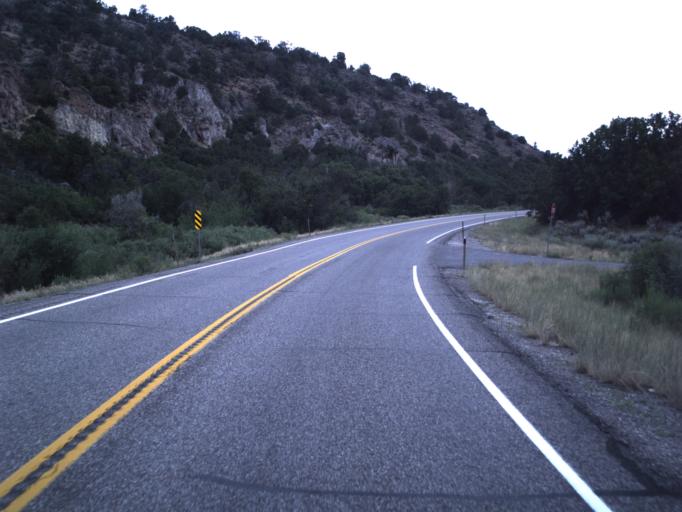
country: US
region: Utah
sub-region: Sevier County
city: Richfield
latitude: 38.7360
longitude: -111.9157
